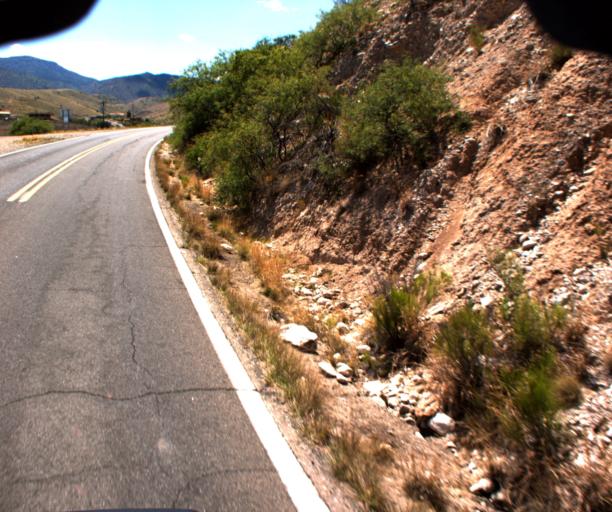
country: US
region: Arizona
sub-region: Yavapai County
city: Clarkdale
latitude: 34.7601
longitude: -112.0658
